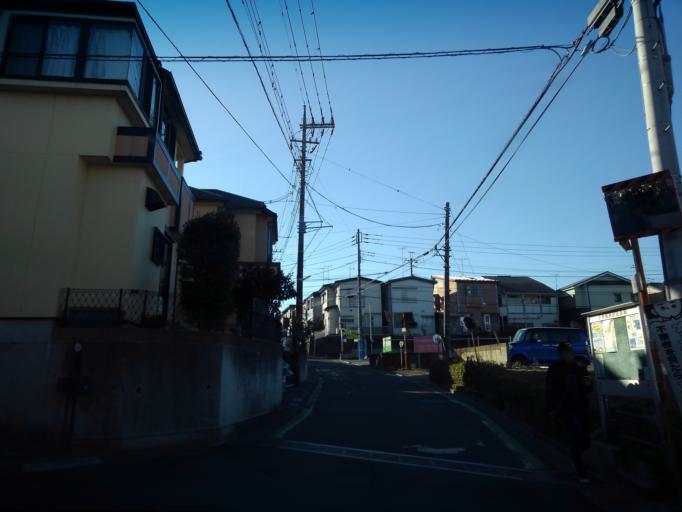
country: JP
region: Saitama
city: Tokorozawa
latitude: 35.7924
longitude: 139.4326
